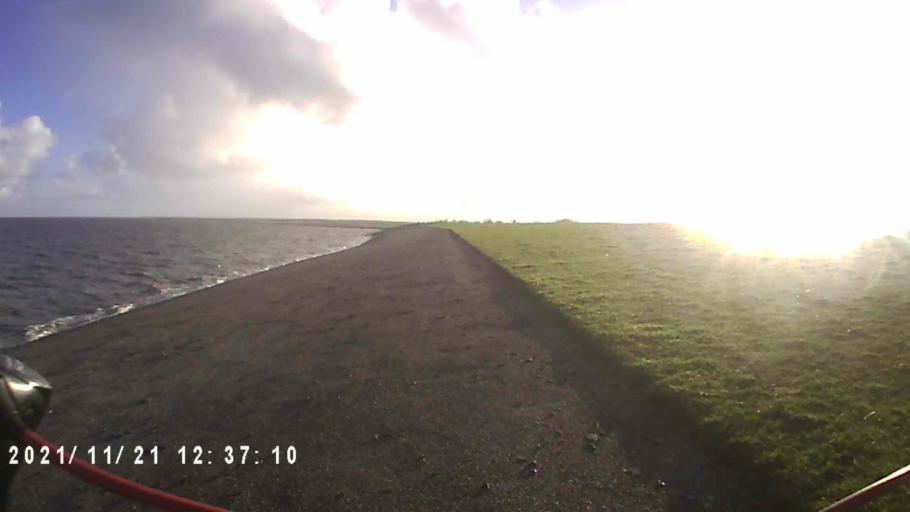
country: NL
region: Friesland
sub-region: Gemeente Dongeradeel
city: Anjum
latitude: 53.4067
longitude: 6.0713
